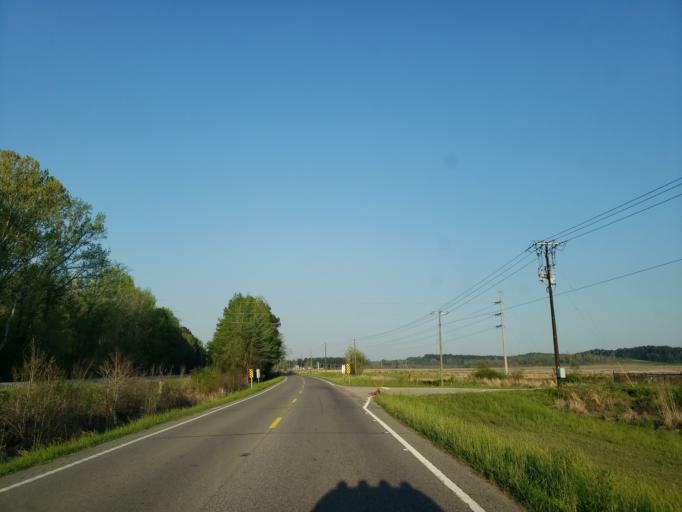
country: US
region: Mississippi
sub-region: Lauderdale County
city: Marion
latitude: 32.3941
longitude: -88.6291
